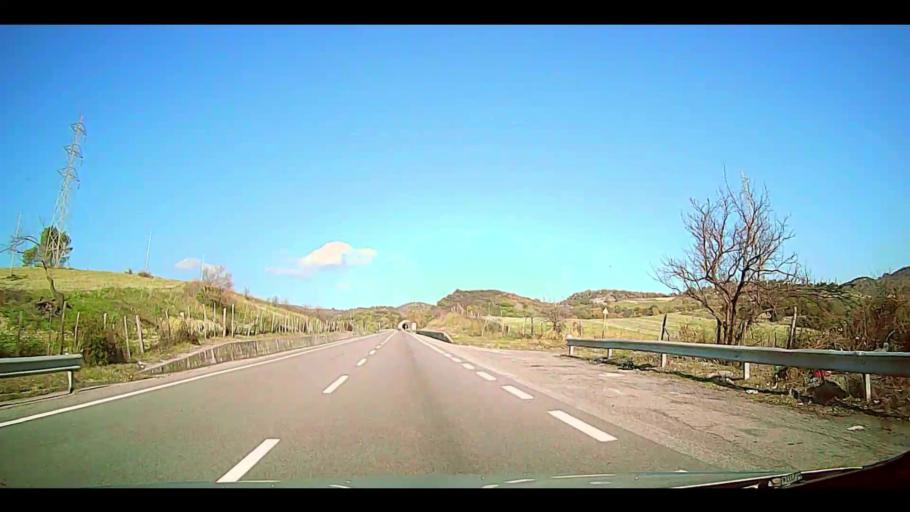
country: IT
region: Calabria
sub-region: Provincia di Crotone
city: Cotronei
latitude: 39.1905
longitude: 16.8156
